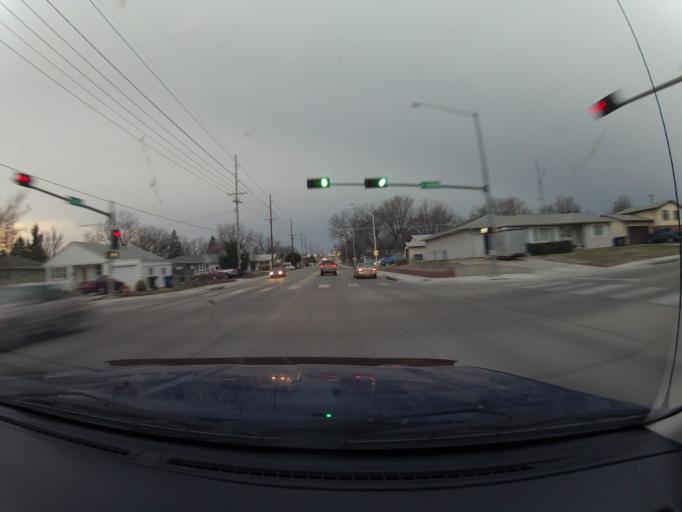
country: US
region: Nebraska
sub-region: Buffalo County
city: Kearney
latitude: 40.7139
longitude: -99.0742
